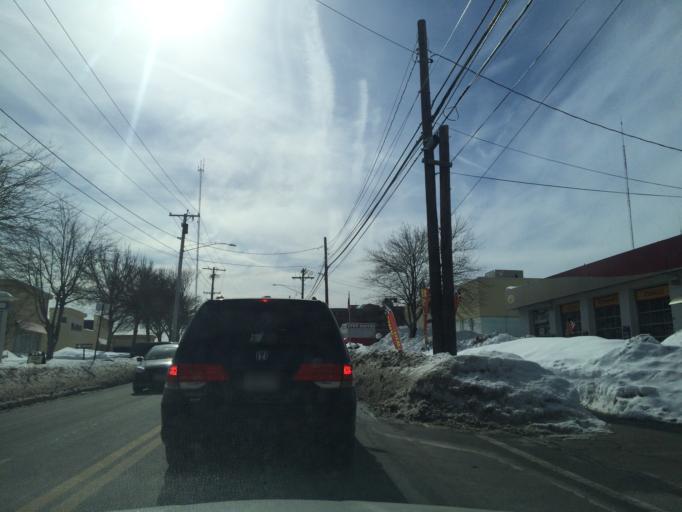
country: US
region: Massachusetts
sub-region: Middlesex County
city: Newton
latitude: 42.3114
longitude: -71.2136
